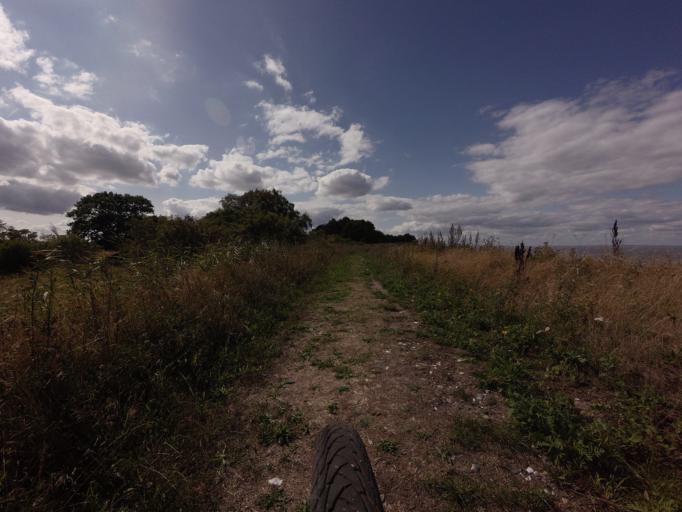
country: DK
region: Zealand
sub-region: Vordingborg Kommune
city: Stege
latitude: 55.0235
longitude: 12.4422
